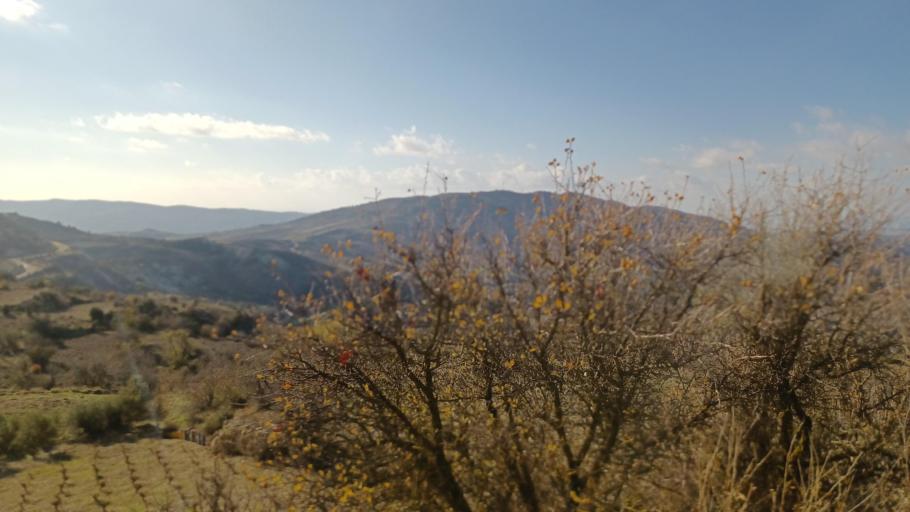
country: CY
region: Limassol
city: Pachna
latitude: 34.8387
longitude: 32.6817
